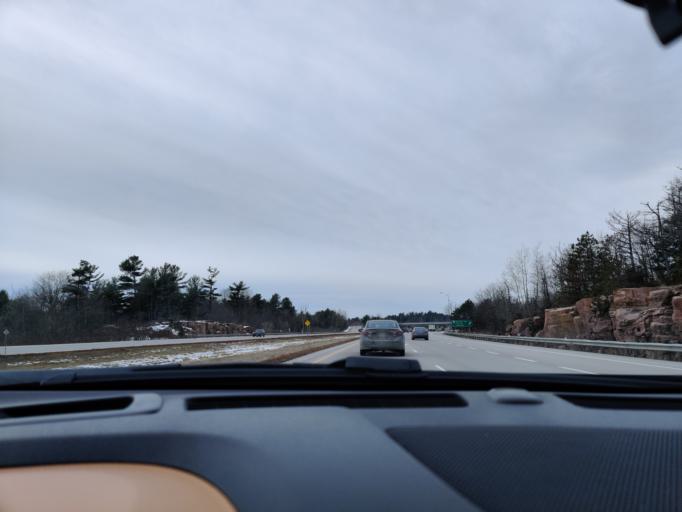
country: US
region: New York
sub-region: Jefferson County
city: Alexandria Bay
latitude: 44.3782
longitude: -76.0015
